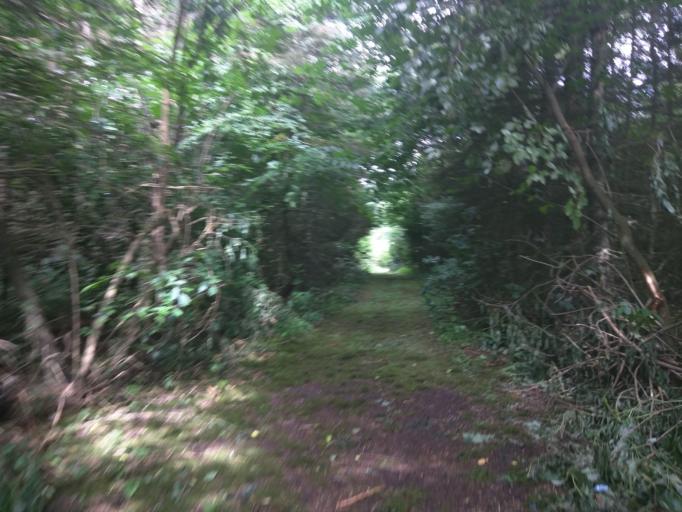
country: DK
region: Zealand
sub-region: Kalundborg Kommune
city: Svebolle
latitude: 55.6722
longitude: 11.3112
